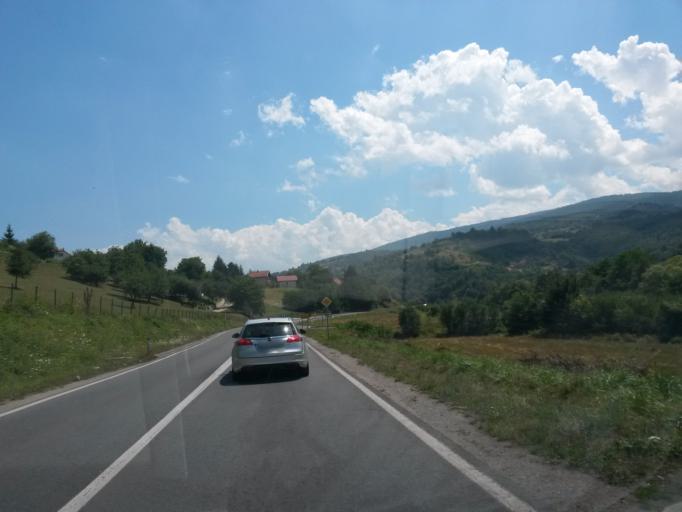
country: BA
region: Federation of Bosnia and Herzegovina
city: Turbe
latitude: 44.2368
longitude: 17.6093
